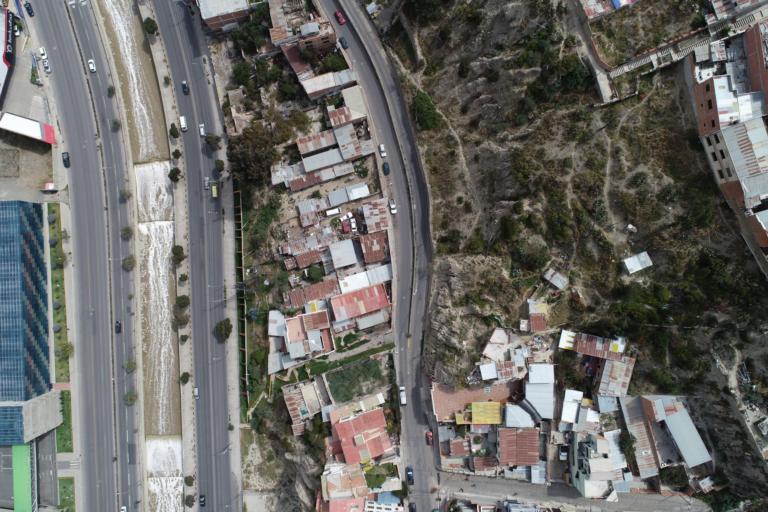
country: BO
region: La Paz
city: La Paz
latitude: -16.5353
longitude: -68.0956
